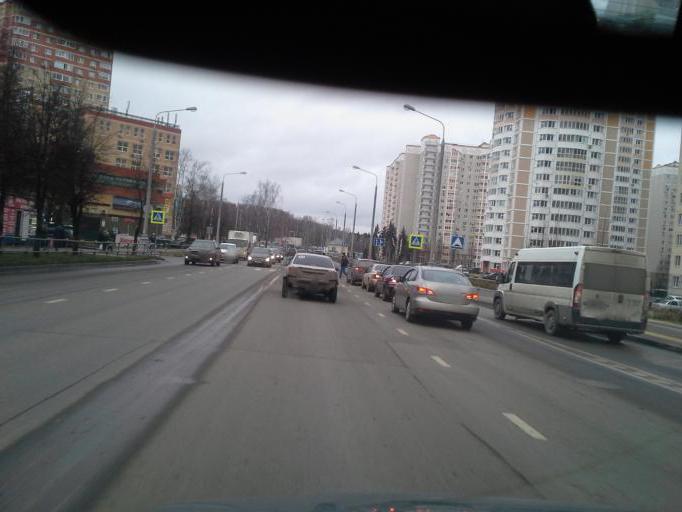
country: RU
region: Moskovskaya
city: Moskovskiy
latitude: 55.6018
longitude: 37.3564
